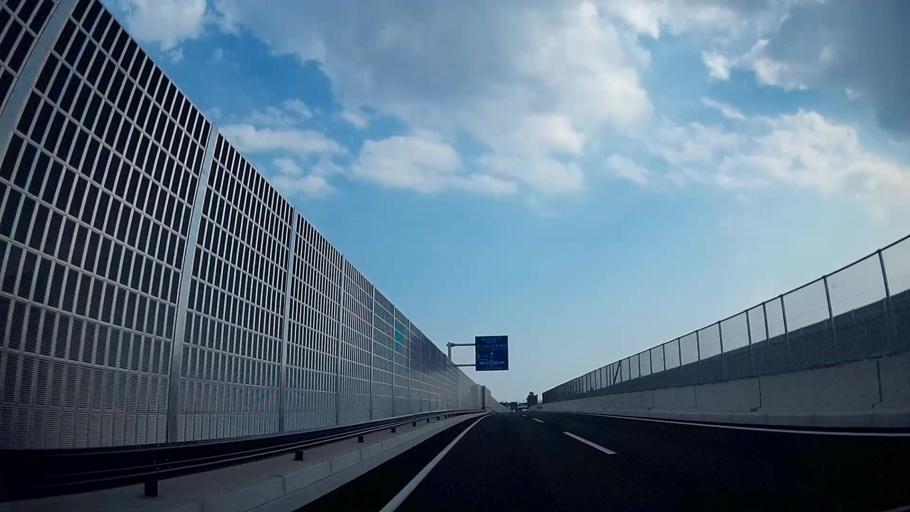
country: JP
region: Chiba
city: Matsudo
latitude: 35.7363
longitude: 139.9205
